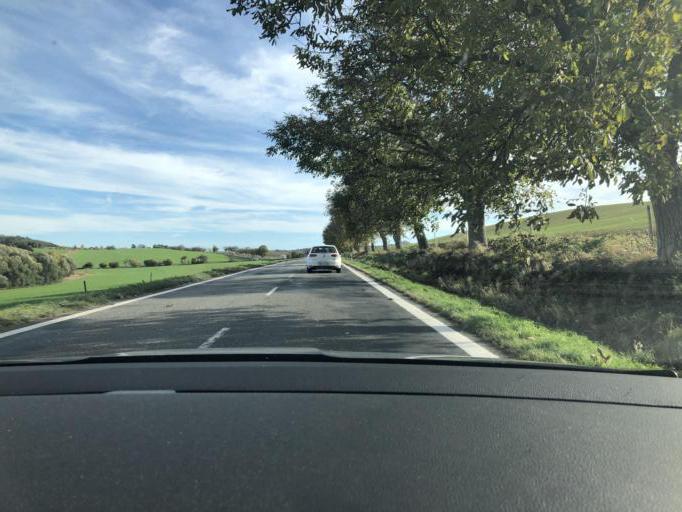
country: CZ
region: Central Bohemia
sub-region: Okres Benesov
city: Benesov
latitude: 49.7760
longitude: 14.7216
